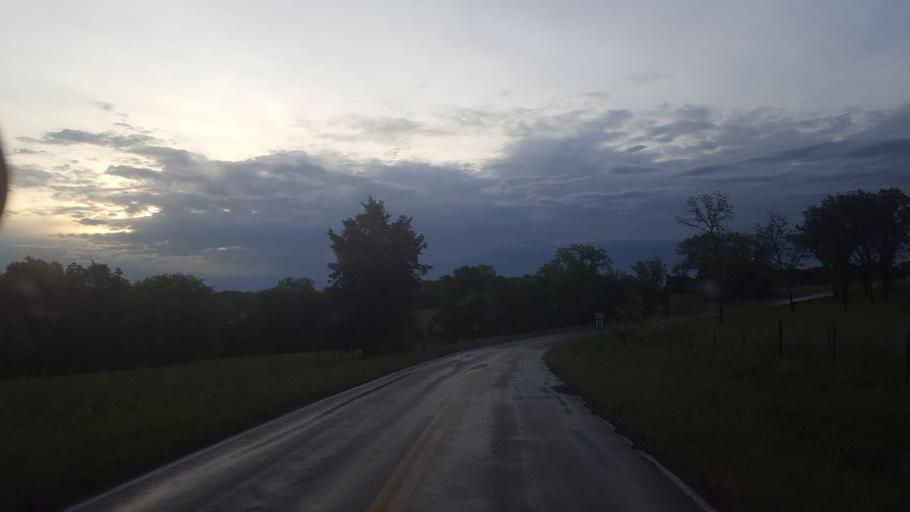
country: US
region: Missouri
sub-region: Moniteau County
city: California
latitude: 38.6829
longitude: -92.5884
